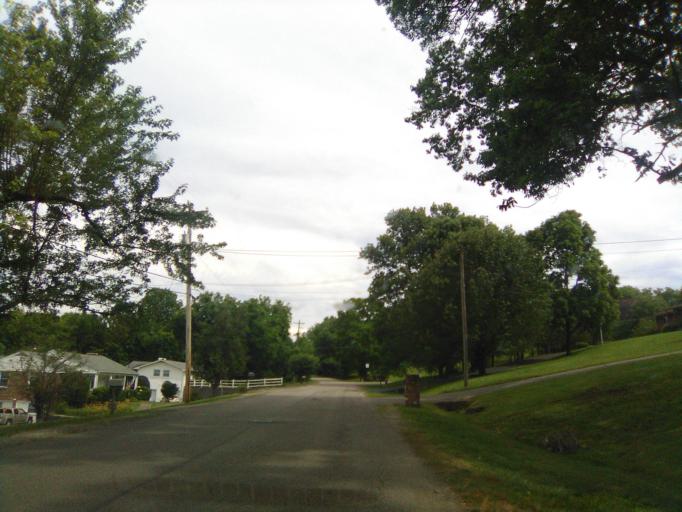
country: US
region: Tennessee
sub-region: Davidson County
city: Belle Meade
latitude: 36.1169
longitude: -86.9009
